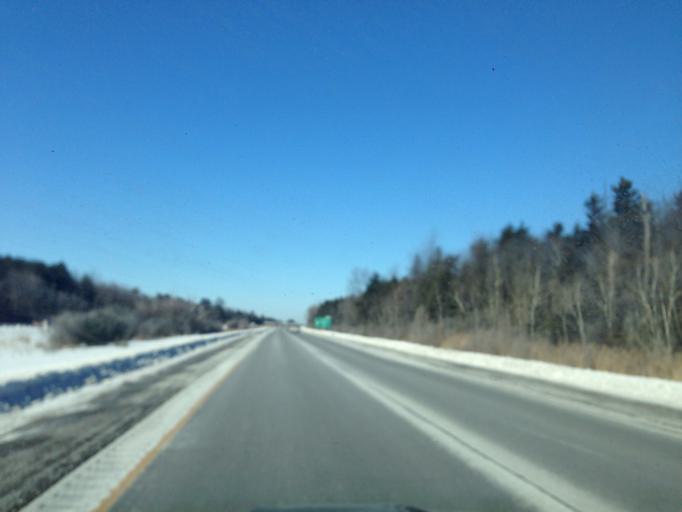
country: CA
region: Ontario
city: Ottawa
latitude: 45.3664
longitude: -75.5212
